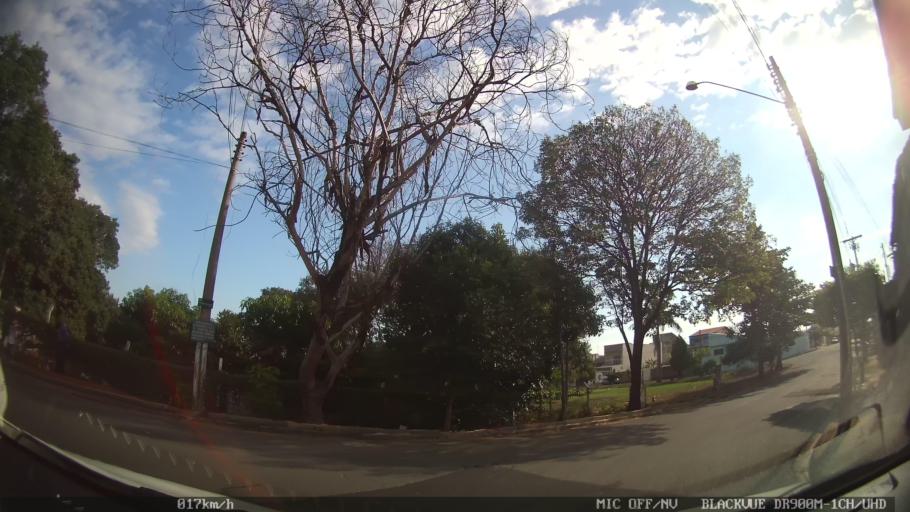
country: BR
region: Sao Paulo
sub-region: Americana
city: Americana
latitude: -22.7221
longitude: -47.3695
